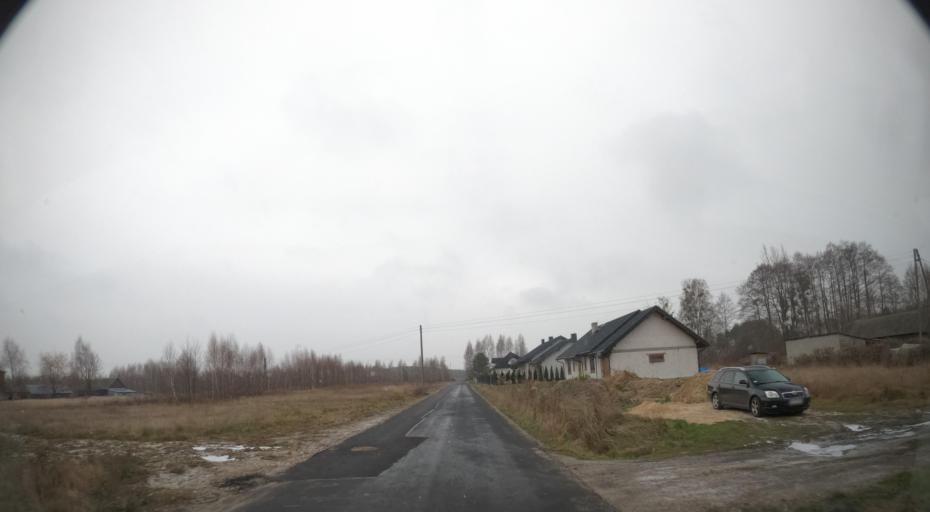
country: PL
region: Masovian Voivodeship
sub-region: Powiat radomski
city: Jedlnia-Letnisko
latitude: 51.4045
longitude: 21.2778
